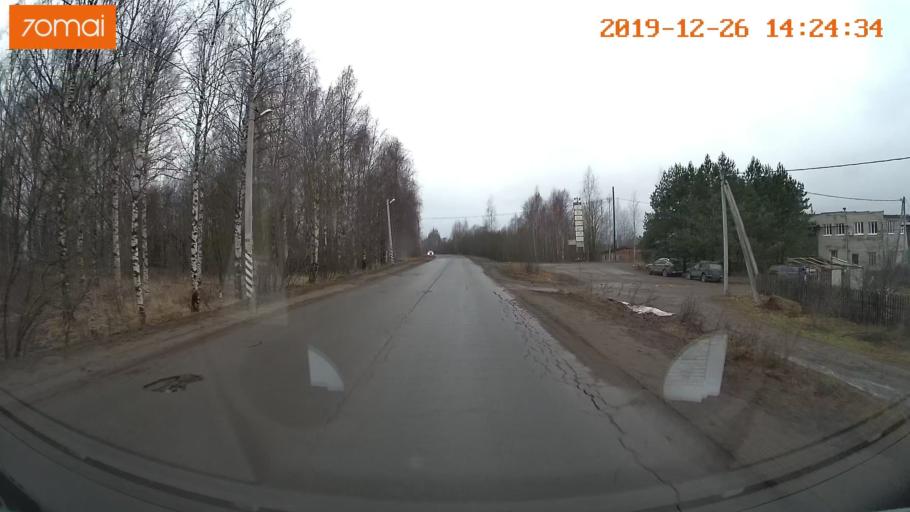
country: RU
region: Jaroslavl
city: Poshekhon'ye
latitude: 58.4982
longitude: 39.1050
